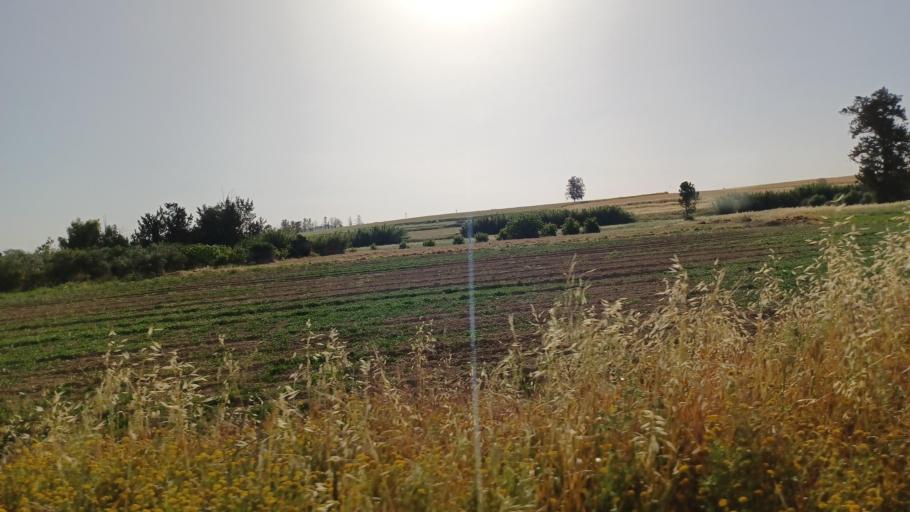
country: CY
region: Lefkosia
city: Mammari
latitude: 35.1580
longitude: 33.2477
